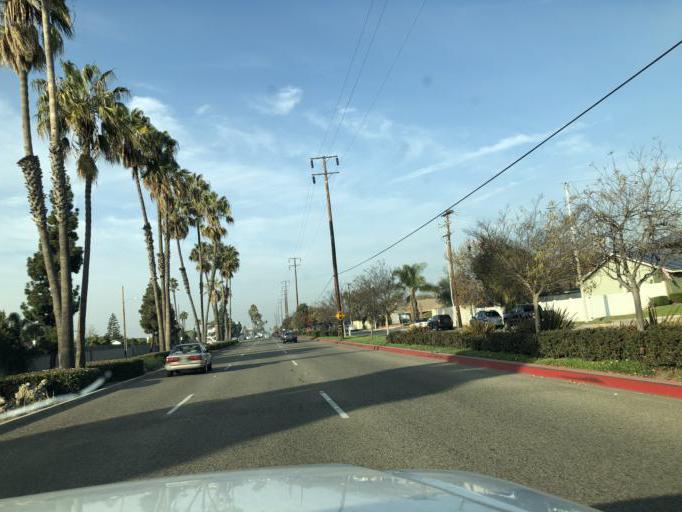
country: US
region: California
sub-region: Orange County
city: Fountain Valley
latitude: 33.6776
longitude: -117.9539
